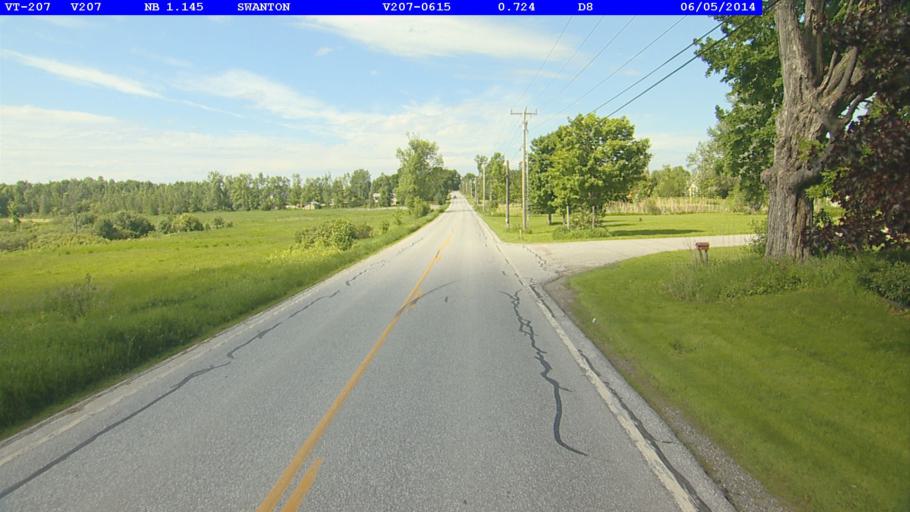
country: US
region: Vermont
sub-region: Franklin County
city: Saint Albans
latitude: 44.8554
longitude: -73.0750
